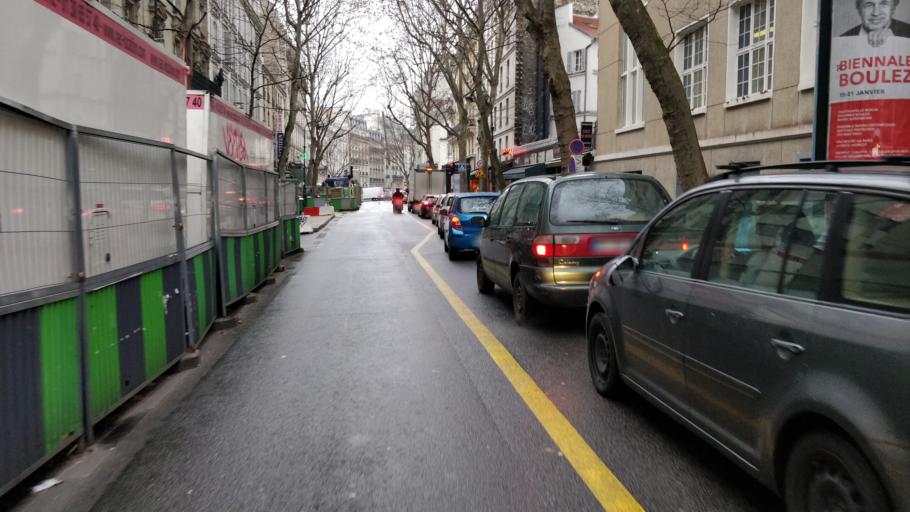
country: FR
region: Ile-de-France
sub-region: Departement de Seine-Saint-Denis
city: Le Pre-Saint-Gervais
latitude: 48.8738
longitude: 2.3870
